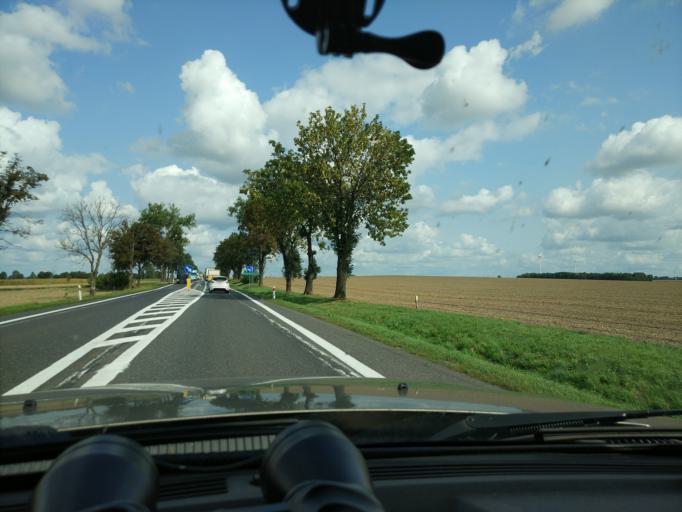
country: PL
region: Masovian Voivodeship
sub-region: Powiat mlawski
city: Wisniewo
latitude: 53.0417
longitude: 20.3411
